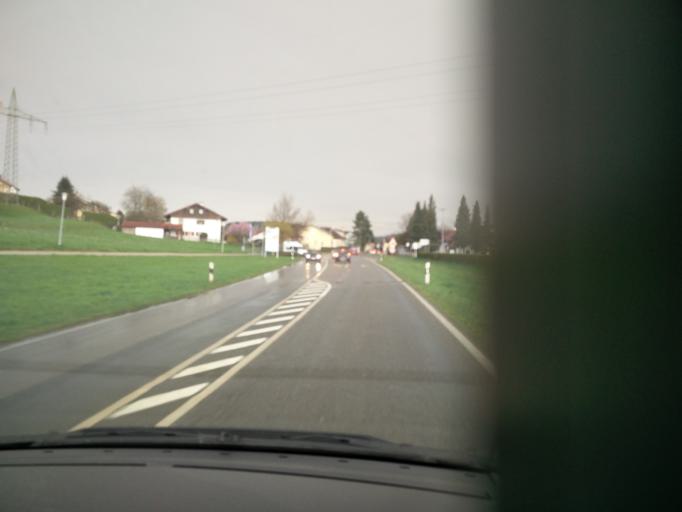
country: DE
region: Bavaria
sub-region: Upper Bavaria
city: Bad Endorf
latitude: 47.9129
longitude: 12.2946
